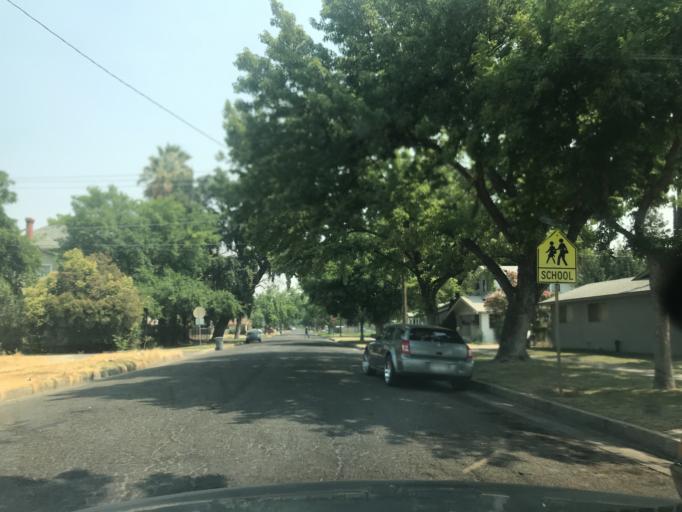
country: US
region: California
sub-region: Merced County
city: Merced
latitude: 37.3080
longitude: -120.4778
